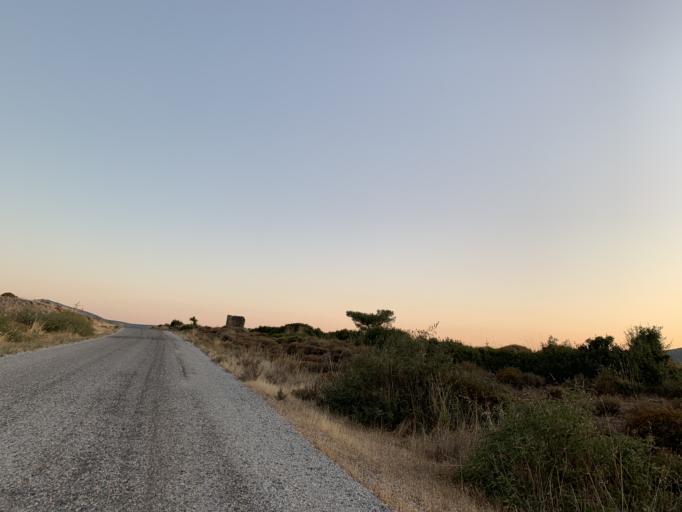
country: TR
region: Izmir
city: Uzunkuyu
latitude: 38.3288
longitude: 26.5841
